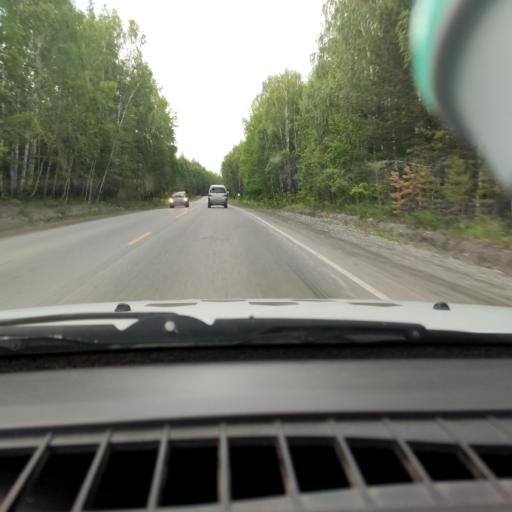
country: RU
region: Chelyabinsk
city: Karabash
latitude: 55.5163
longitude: 60.3253
